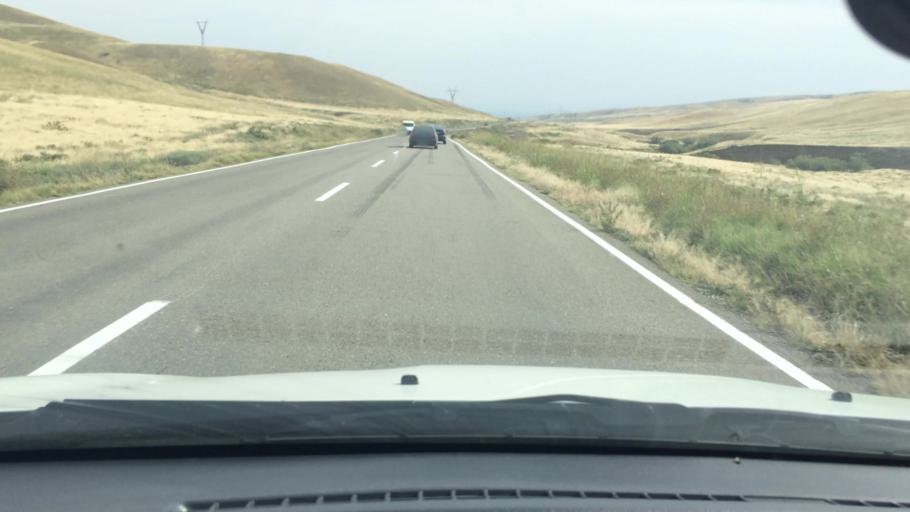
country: GE
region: Kvemo Kartli
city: Rust'avi
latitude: 41.5156
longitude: 44.9445
